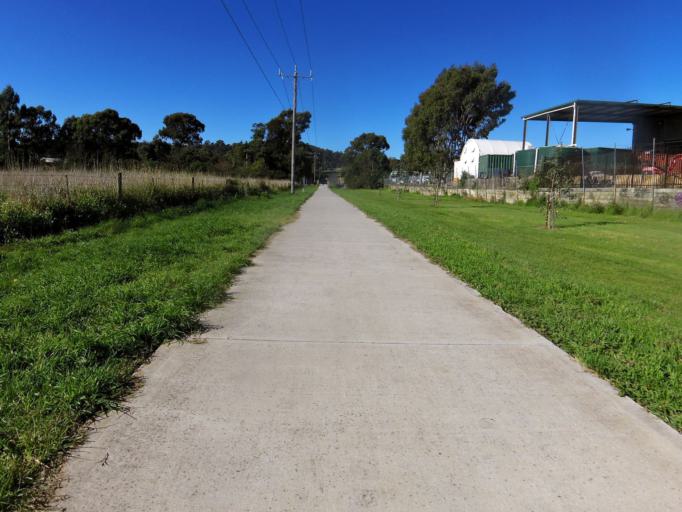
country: AU
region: Victoria
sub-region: Yarra Ranges
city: Lilydale
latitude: -37.7473
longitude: 145.3521
